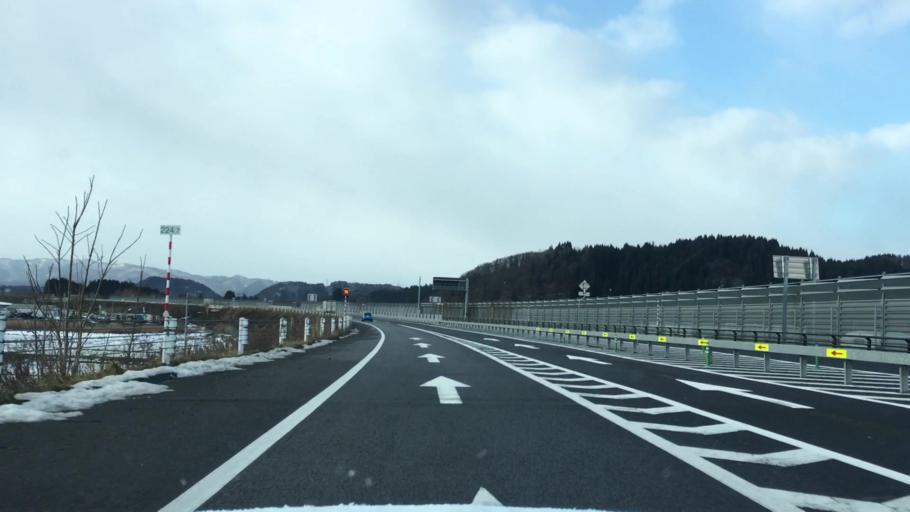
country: JP
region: Akita
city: Odate
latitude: 40.3020
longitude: 140.5594
